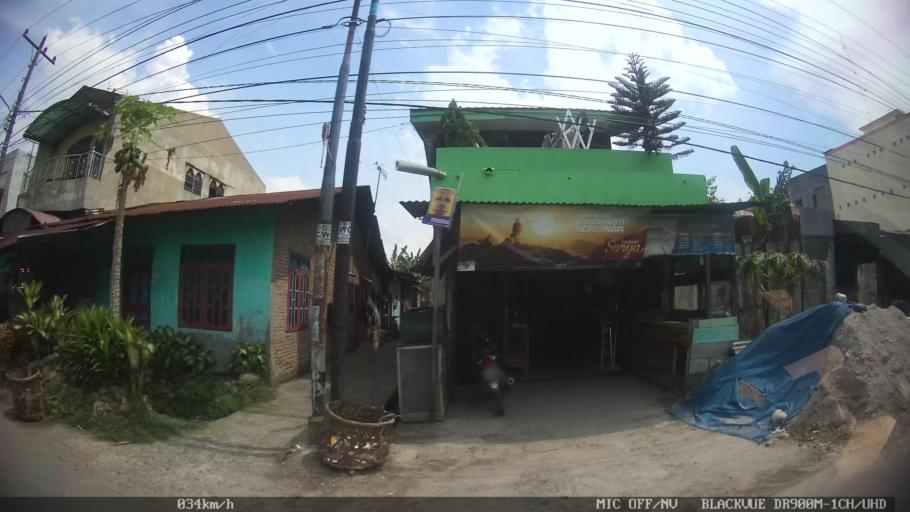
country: ID
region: North Sumatra
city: Labuhan Deli
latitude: 3.6571
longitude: 98.6700
